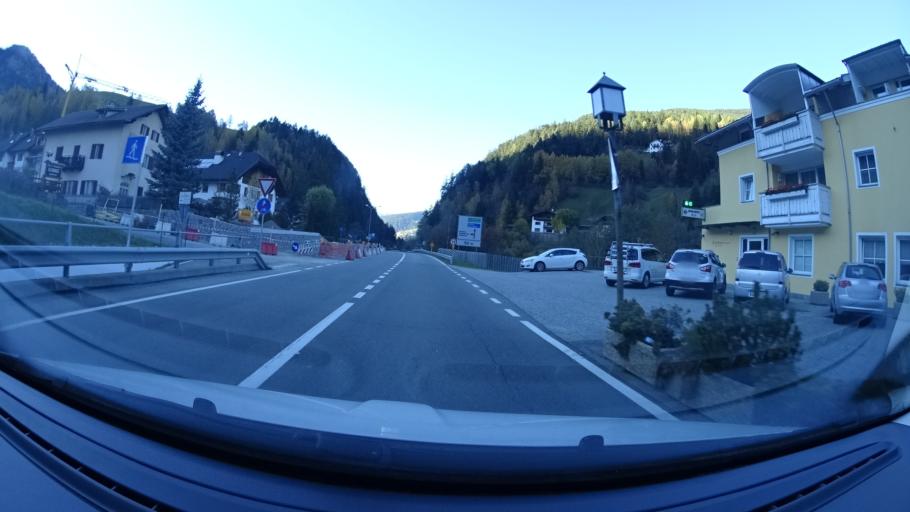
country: IT
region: Trentino-Alto Adige
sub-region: Bolzano
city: Ortisei
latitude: 46.5744
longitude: 11.6463
